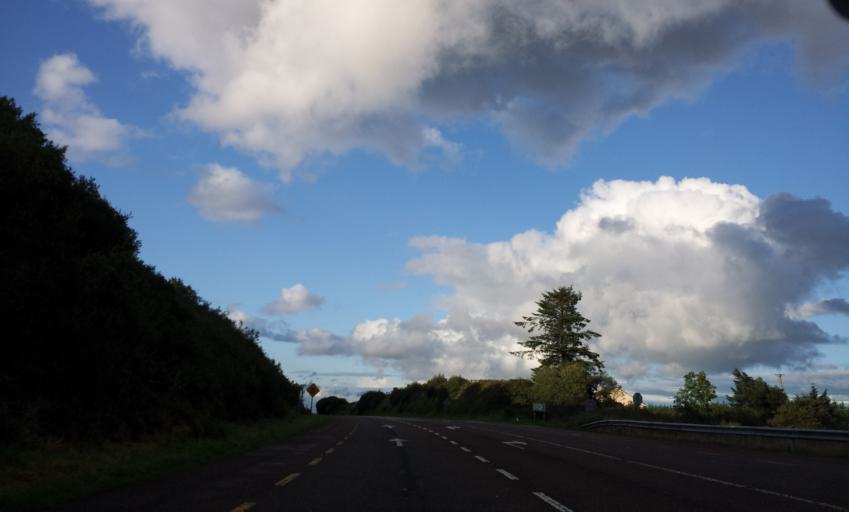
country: IE
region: Munster
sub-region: Ciarrai
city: Castleisland
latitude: 52.2703
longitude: -9.4193
